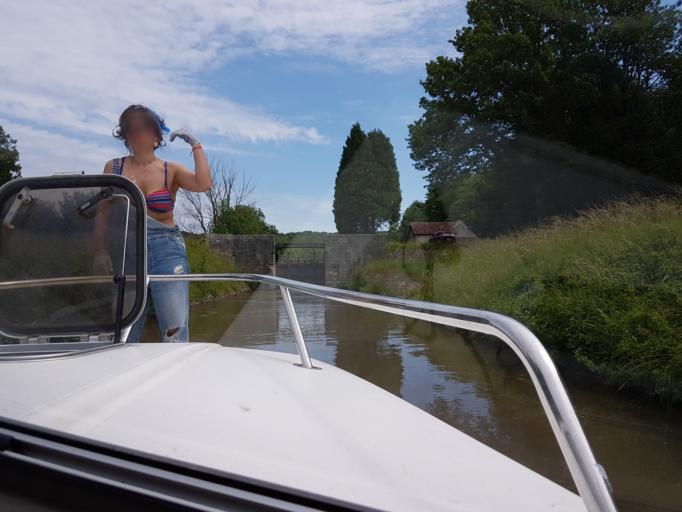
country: FR
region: Bourgogne
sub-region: Departement de la Nievre
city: Clamecy
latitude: 47.4526
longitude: 3.5383
